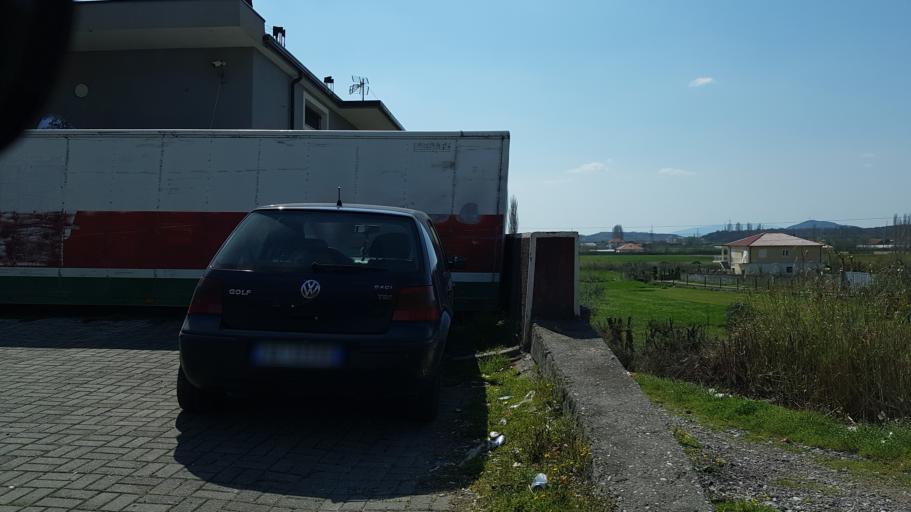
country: AL
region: Shkoder
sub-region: Rrethi i Shkodres
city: Guri i Zi
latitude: 42.0210
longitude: 19.5775
